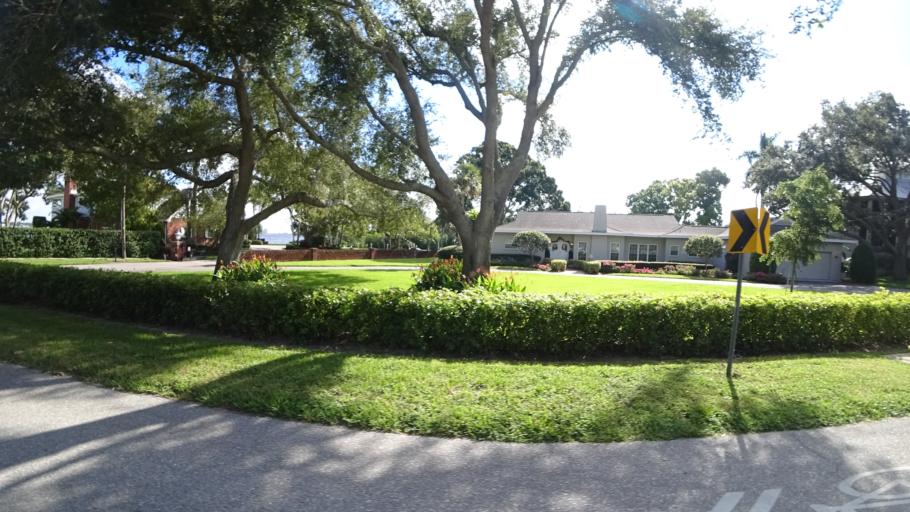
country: US
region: Florida
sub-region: Manatee County
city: West Bradenton
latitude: 27.5030
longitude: -82.5999
